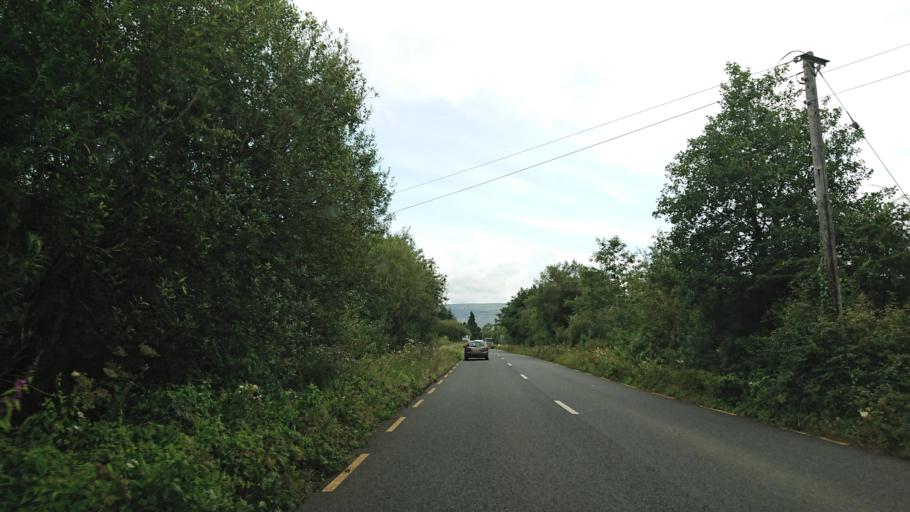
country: IE
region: Connaught
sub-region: County Leitrim
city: Carrick-on-Shannon
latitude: 54.0655
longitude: -8.0871
